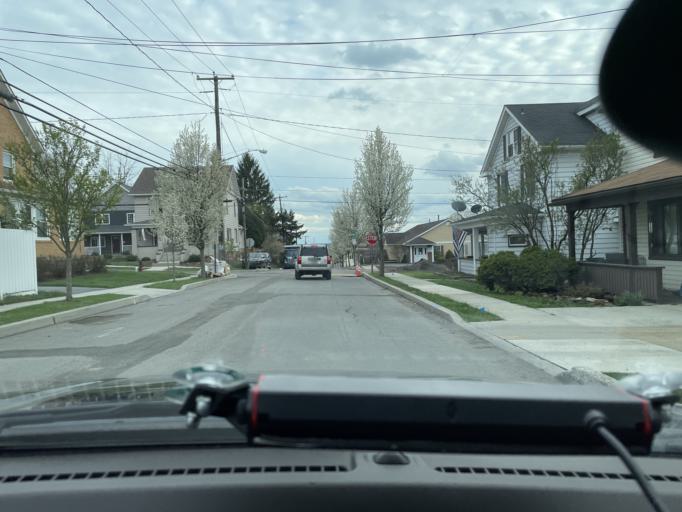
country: US
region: Pennsylvania
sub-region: Cambria County
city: Ebensburg
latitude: 40.4864
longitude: -78.7293
